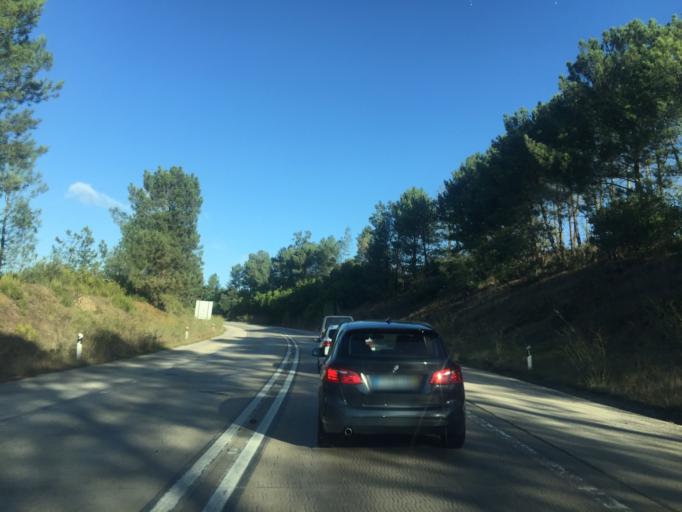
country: PT
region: Santarem
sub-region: Rio Maior
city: Rio Maior
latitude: 39.3168
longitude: -8.9366
